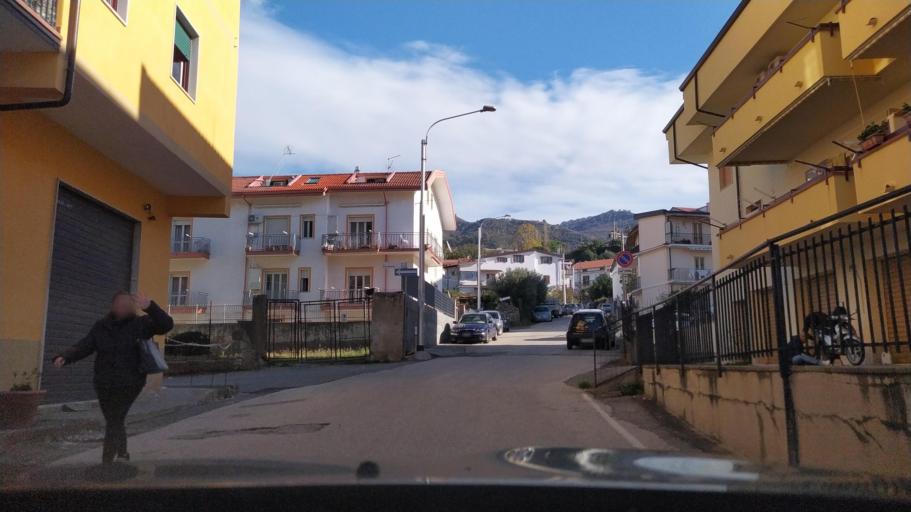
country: IT
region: Calabria
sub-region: Provincia di Cosenza
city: Paola
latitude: 39.3686
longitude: 16.0293
